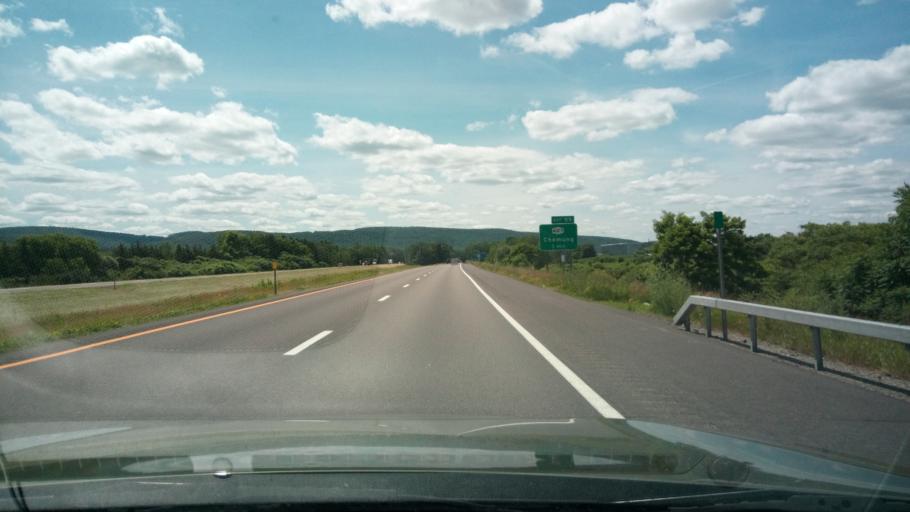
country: US
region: Pennsylvania
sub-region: Bradford County
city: South Waverly
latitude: 42.0013
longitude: -76.6060
